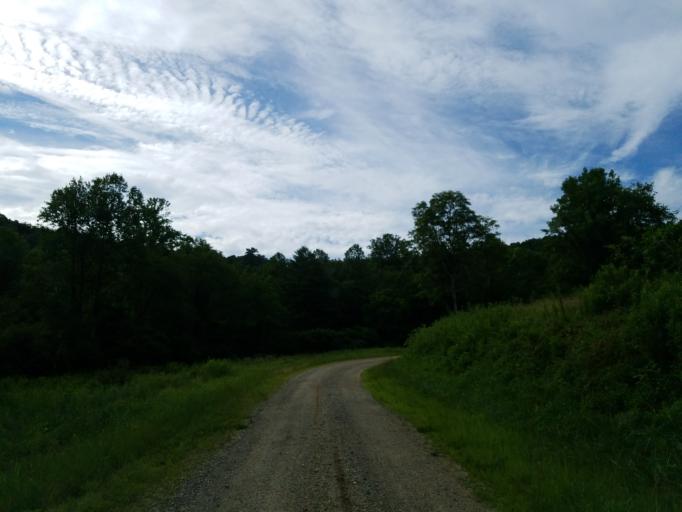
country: US
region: Georgia
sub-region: Union County
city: Blairsville
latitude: 34.7274
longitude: -84.0596
